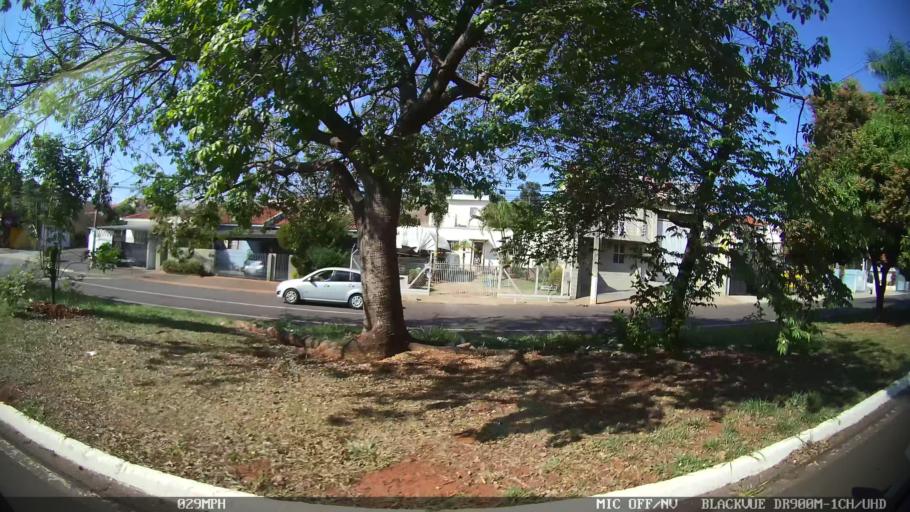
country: BR
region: Sao Paulo
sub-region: Americana
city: Americana
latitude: -22.7543
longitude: -47.3261
